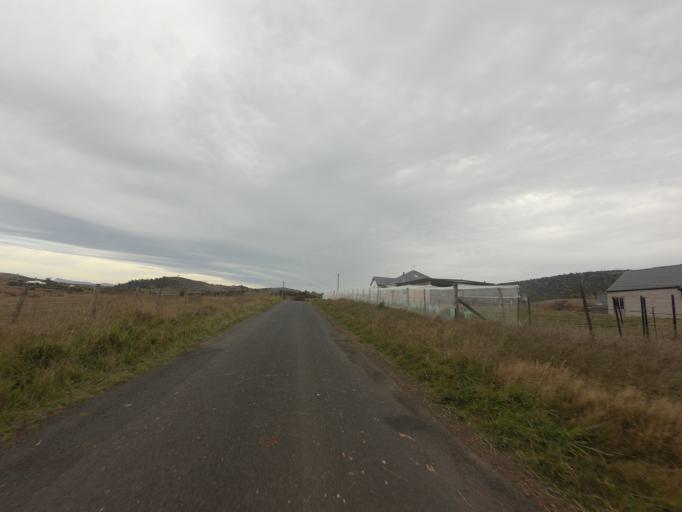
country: AU
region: Tasmania
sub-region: Derwent Valley
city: New Norfolk
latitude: -42.5342
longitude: 146.9403
